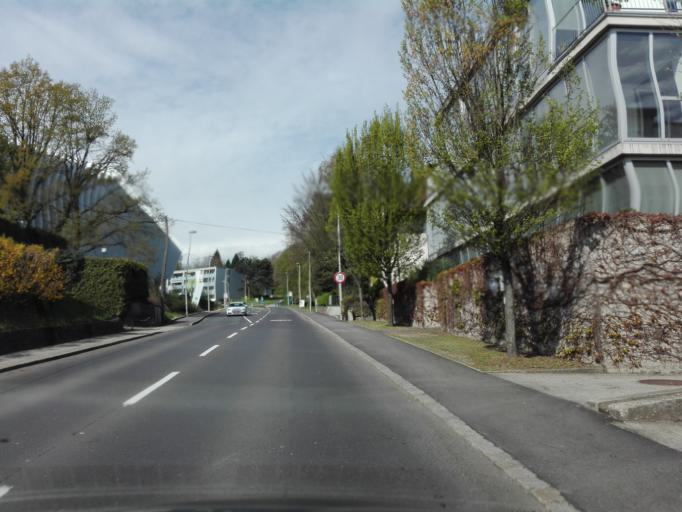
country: AT
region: Upper Austria
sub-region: Linz Stadt
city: Linz
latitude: 48.3113
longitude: 14.2710
